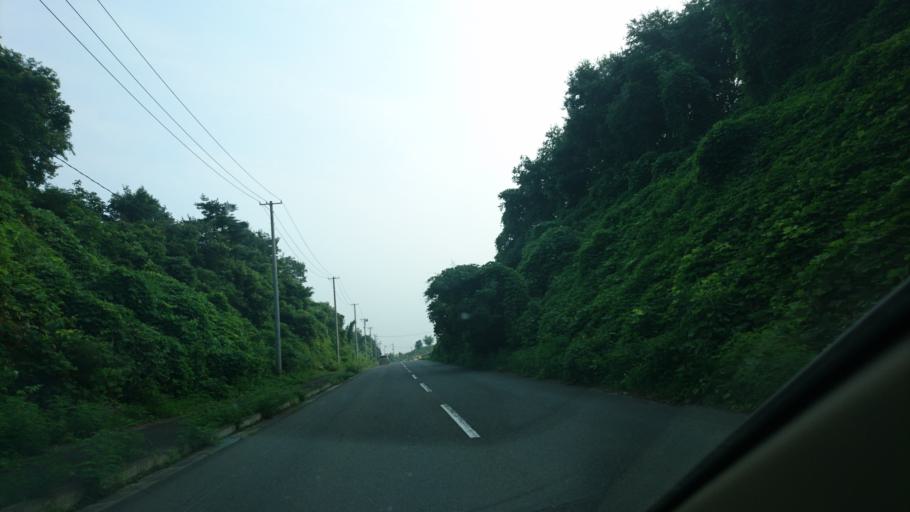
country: JP
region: Iwate
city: Kitakami
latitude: 39.2216
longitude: 141.1919
